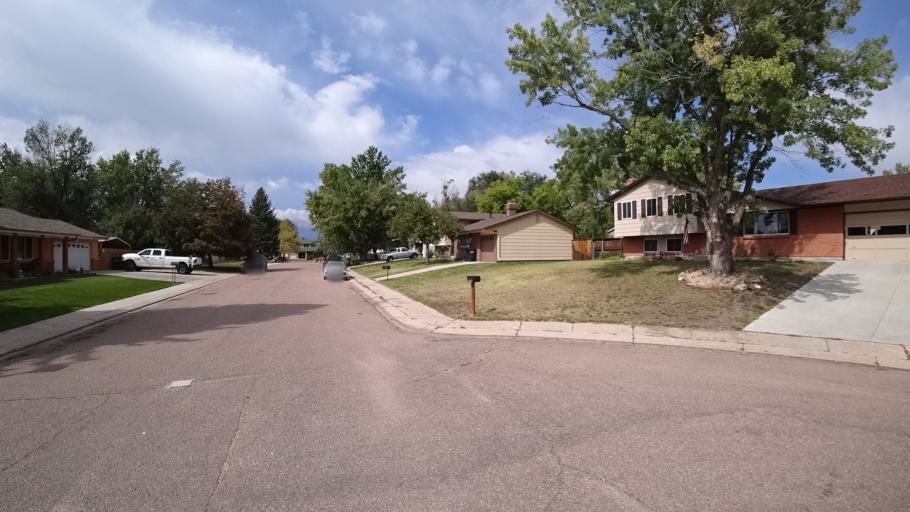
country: US
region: Colorado
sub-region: El Paso County
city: Cimarron Hills
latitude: 38.8503
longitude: -104.7399
